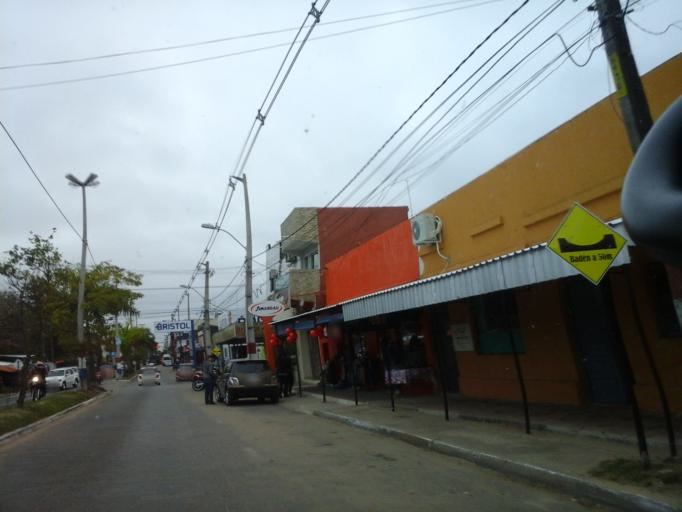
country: PY
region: Neembucu
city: Pilar
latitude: -26.8621
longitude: -58.2997
